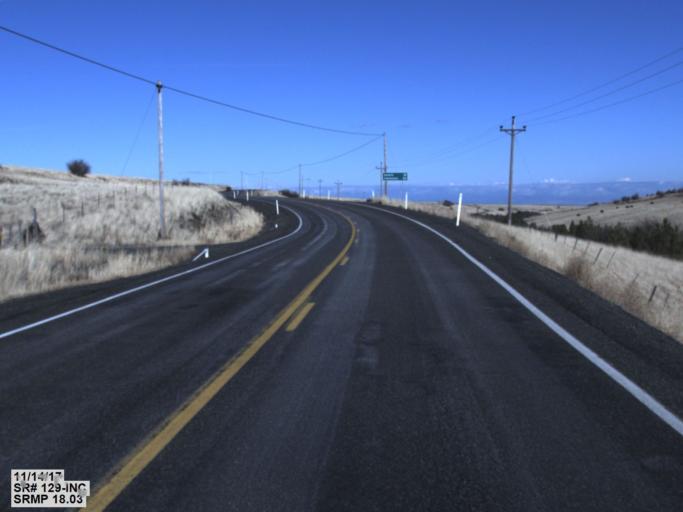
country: US
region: Washington
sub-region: Asotin County
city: Asotin
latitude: 46.1419
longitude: -117.1270
